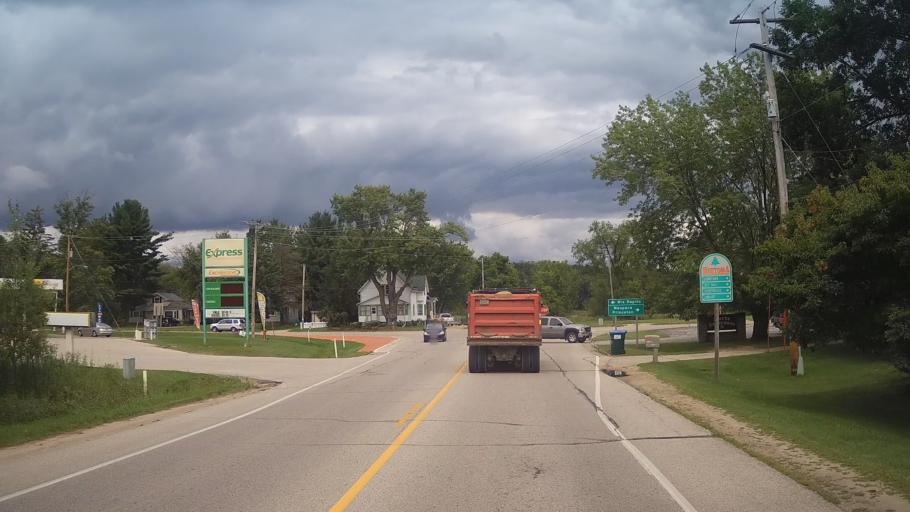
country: US
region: Wisconsin
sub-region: Waushara County
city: Wautoma
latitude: 44.0756
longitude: -89.2963
